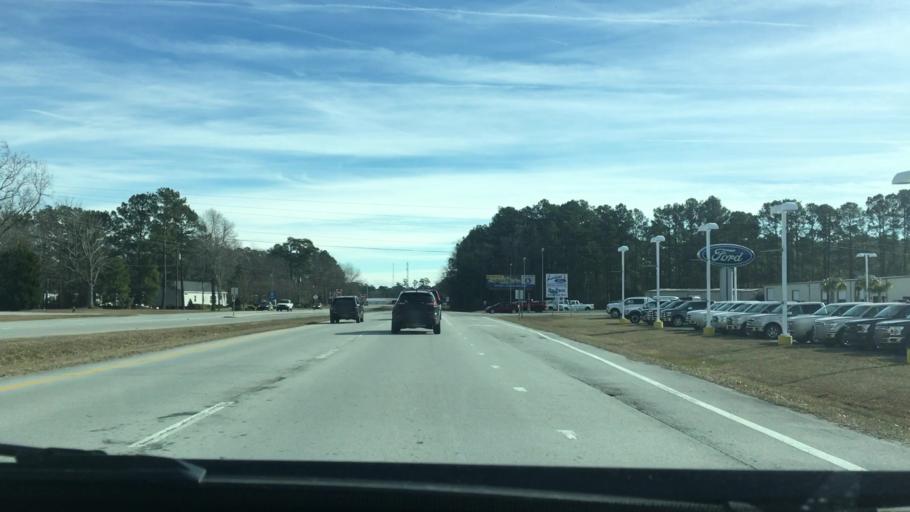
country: US
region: North Carolina
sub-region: Carteret County
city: Newport
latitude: 34.7482
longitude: -76.8366
